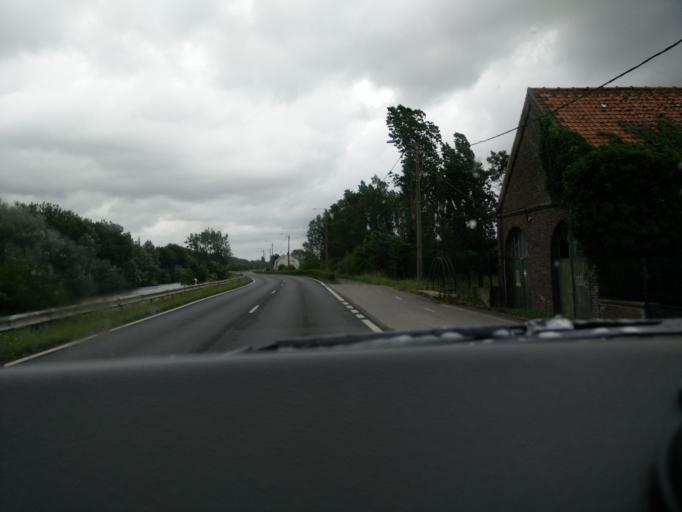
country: FR
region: Nord-Pas-de-Calais
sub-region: Departement du Nord
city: Coudekerque-Village
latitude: 50.9818
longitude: 2.4102
